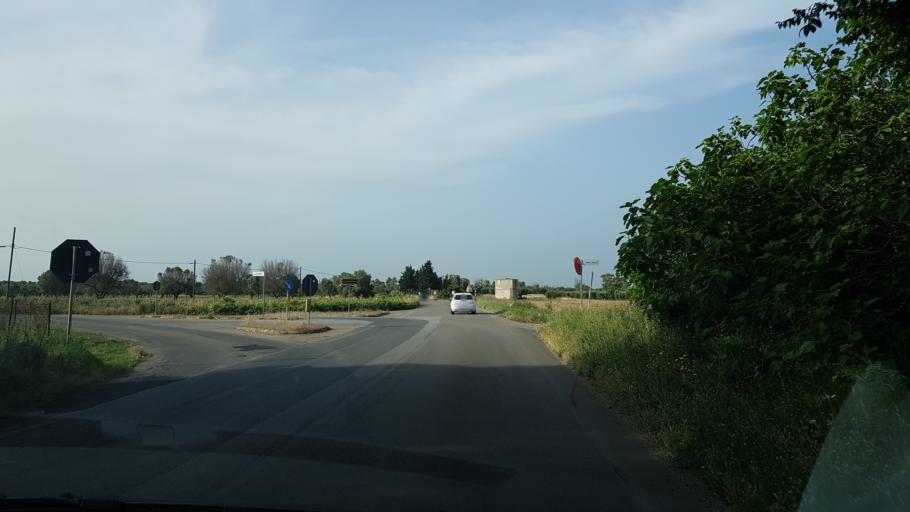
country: IT
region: Apulia
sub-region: Provincia di Lecce
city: Porto Cesareo
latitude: 40.3070
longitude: 17.8625
